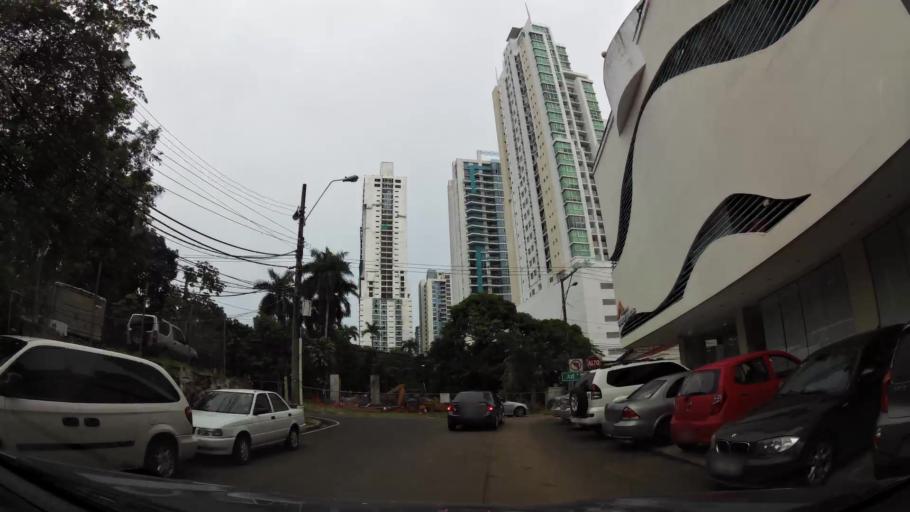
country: PA
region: Panama
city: Panama
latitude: 8.9740
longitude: -79.5308
